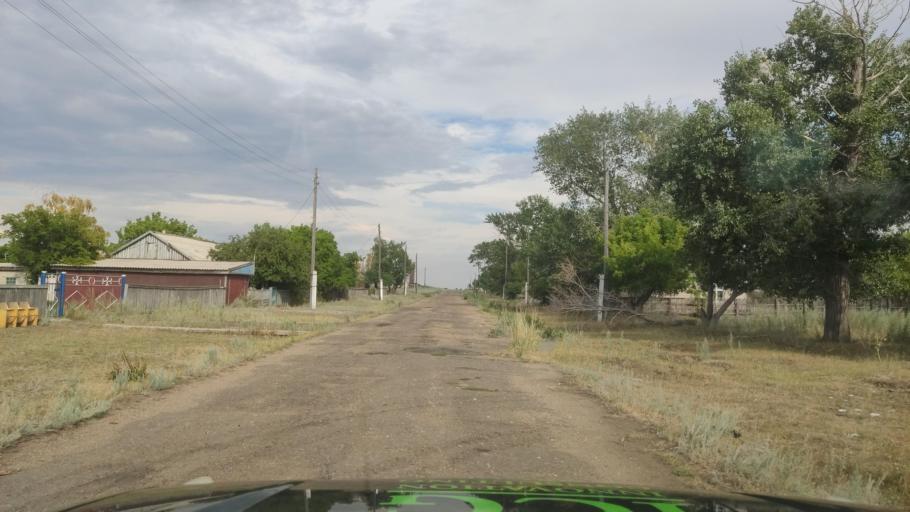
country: KZ
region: Pavlodar
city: Pavlodar
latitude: 52.5005
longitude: 77.5962
